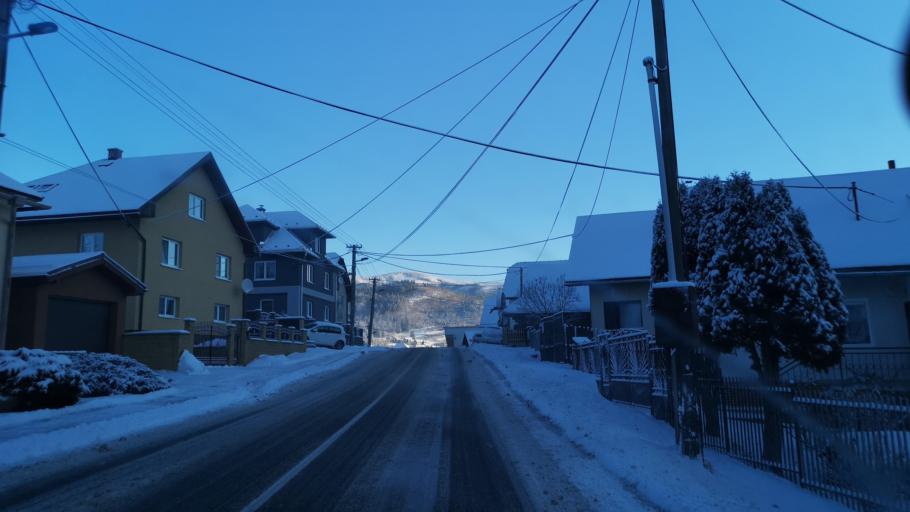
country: SK
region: Banskobystricky
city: Tisovec
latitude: 48.8592
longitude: 19.9668
